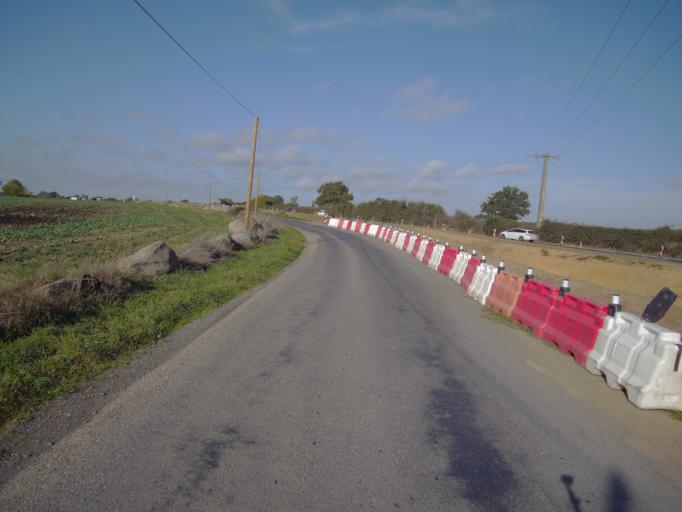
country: FR
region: Pays de la Loire
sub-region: Departement de Maine-et-Loire
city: Coron
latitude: 47.1249
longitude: -0.6629
